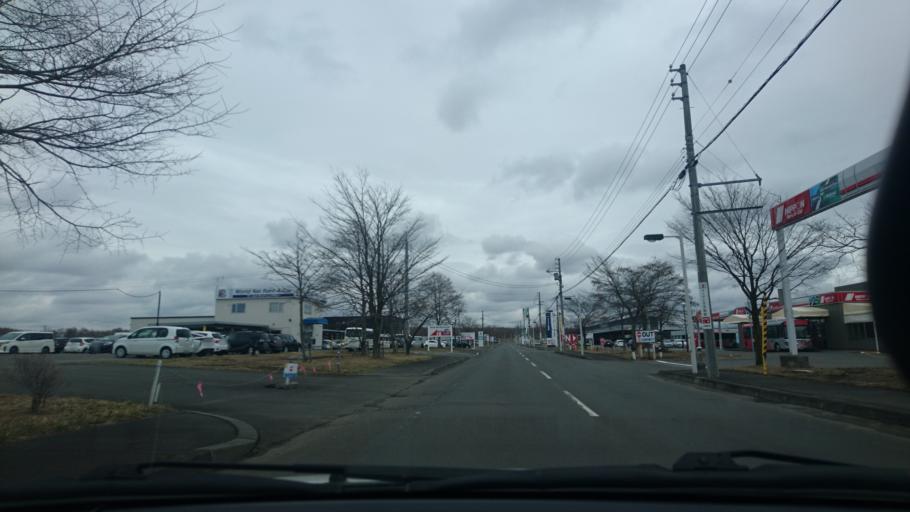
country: JP
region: Hokkaido
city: Chitose
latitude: 42.8000
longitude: 141.6987
